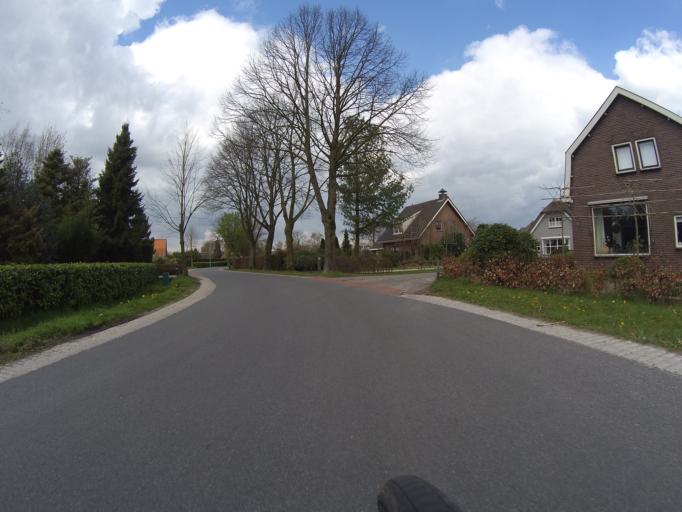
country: NL
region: Gelderland
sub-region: Gemeente Nijkerk
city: Nijkerk
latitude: 52.1910
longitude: 5.4561
